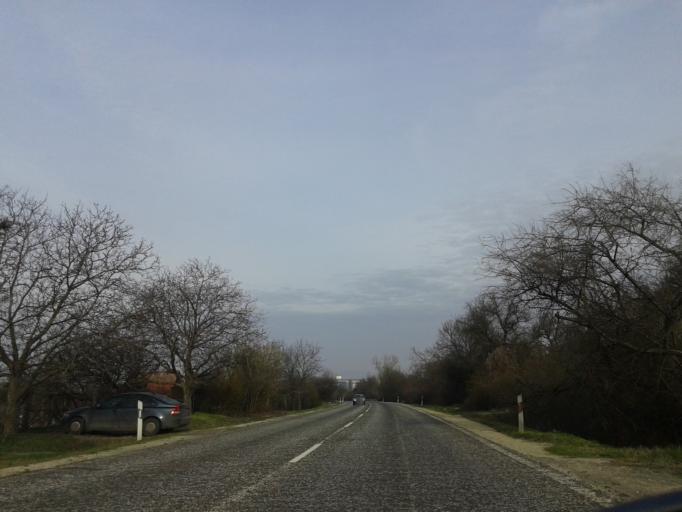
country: HU
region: Pest
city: Biatorbagy
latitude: 47.4867
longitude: 18.8319
